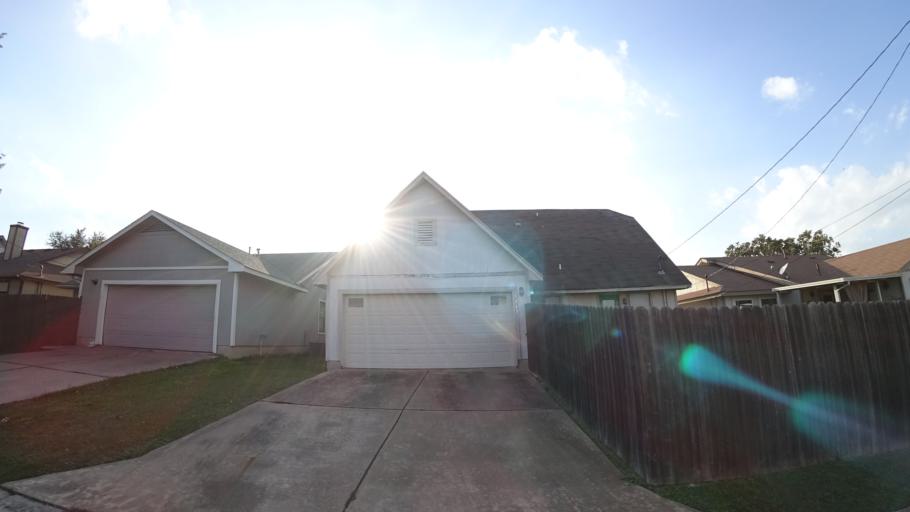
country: US
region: Texas
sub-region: Williamson County
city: Round Rock
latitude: 30.4933
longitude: -97.6638
